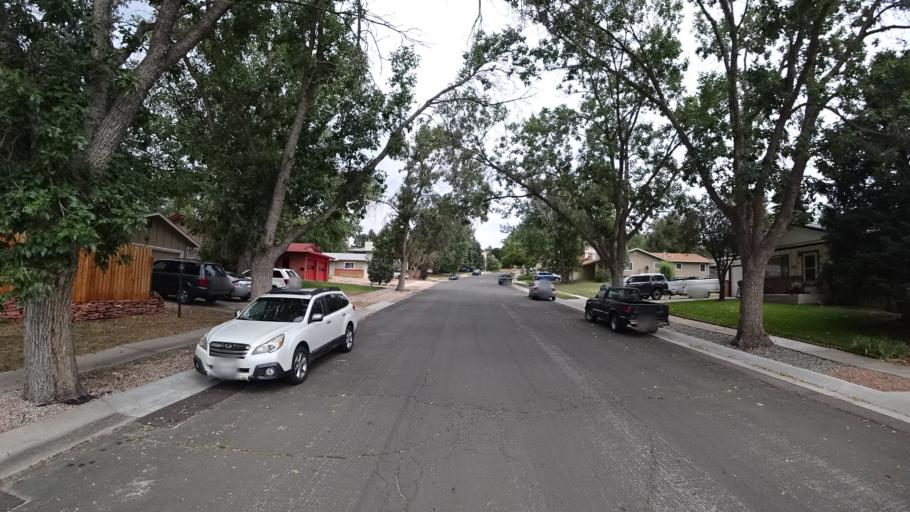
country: US
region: Colorado
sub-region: El Paso County
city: Colorado Springs
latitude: 38.8950
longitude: -104.8098
